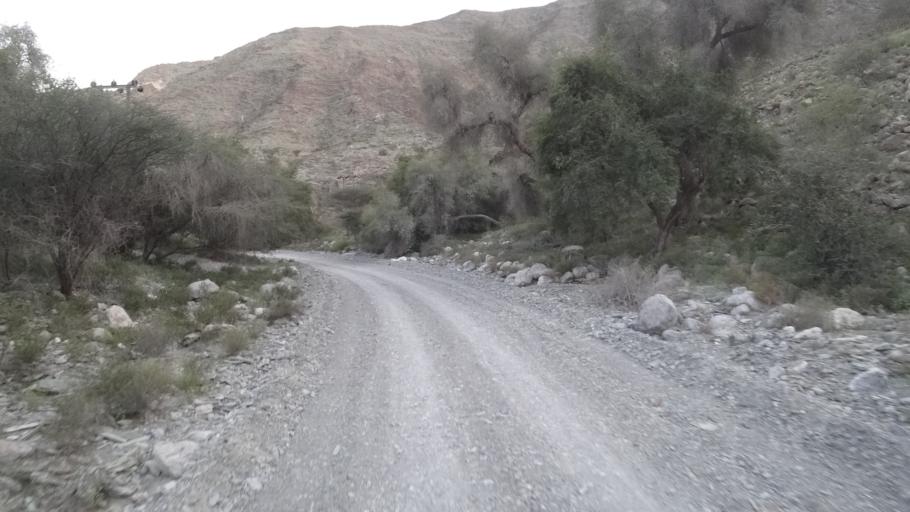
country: OM
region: Al Batinah
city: Bayt al `Awabi
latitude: 23.2355
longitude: 57.4455
